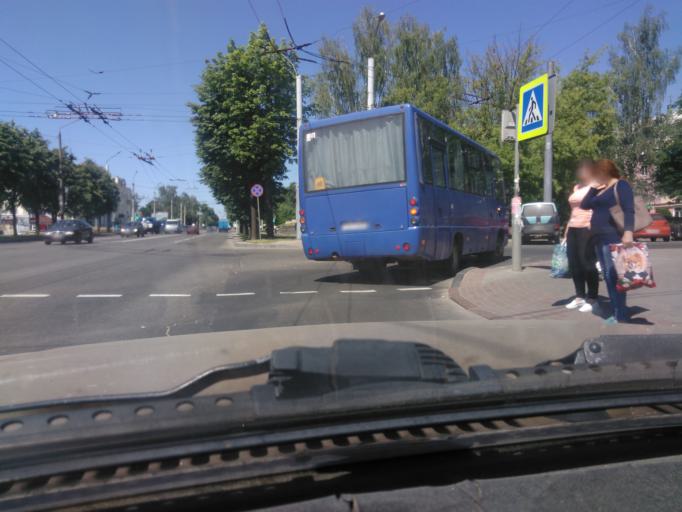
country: BY
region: Mogilev
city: Mahilyow
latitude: 53.9263
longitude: 30.3402
